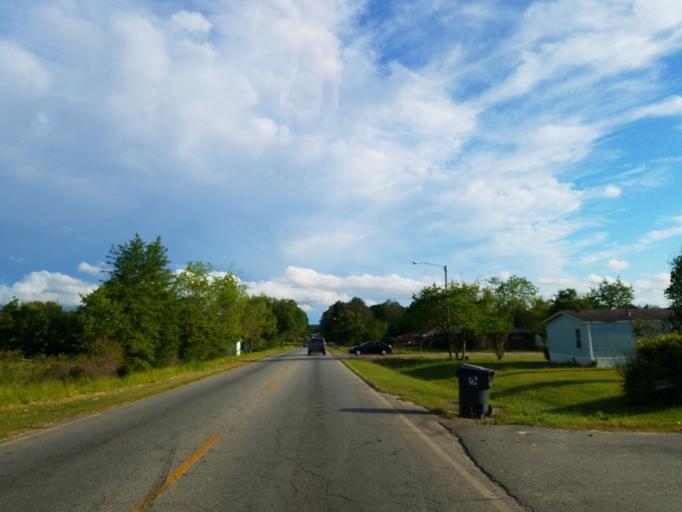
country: US
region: Georgia
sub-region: Crisp County
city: Cordele
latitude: 31.9537
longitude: -83.7878
